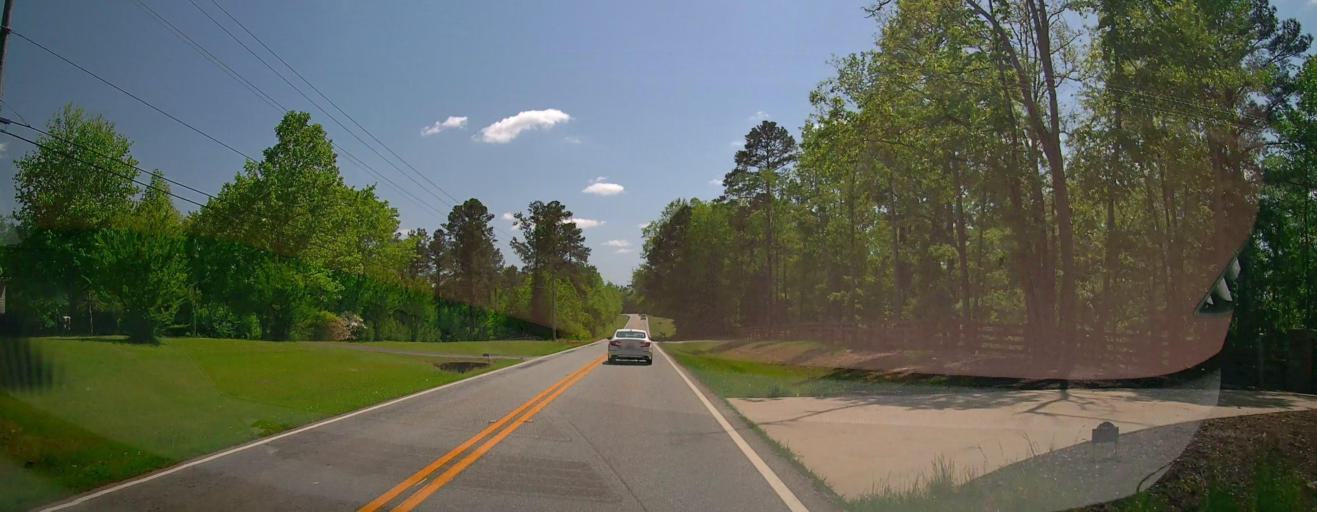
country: US
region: Georgia
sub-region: Putnam County
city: Eatonton
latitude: 33.2863
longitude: -83.3023
